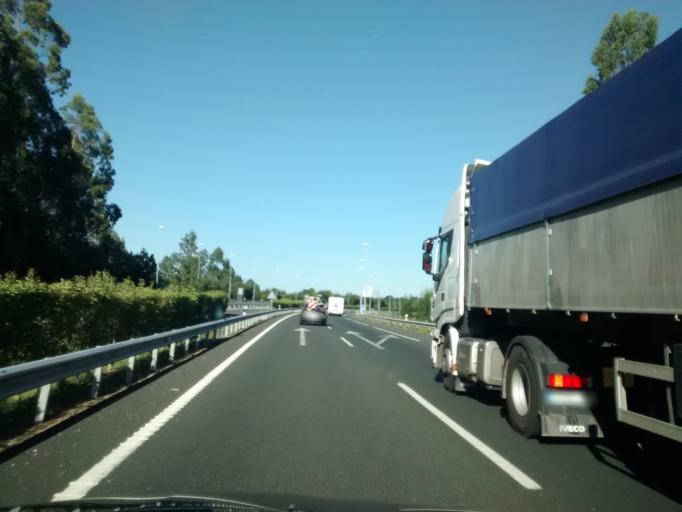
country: ES
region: Cantabria
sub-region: Provincia de Cantabria
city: Reocin
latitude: 43.3429
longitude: -4.1436
